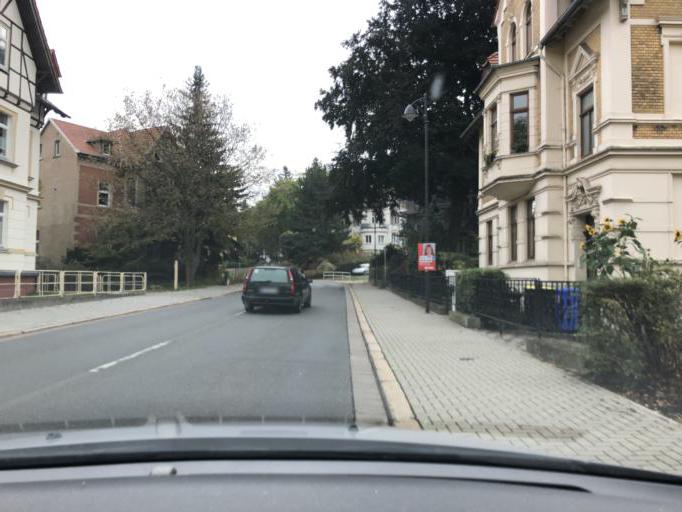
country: DE
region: Thuringia
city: Sondershausen
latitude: 51.3681
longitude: 10.8598
